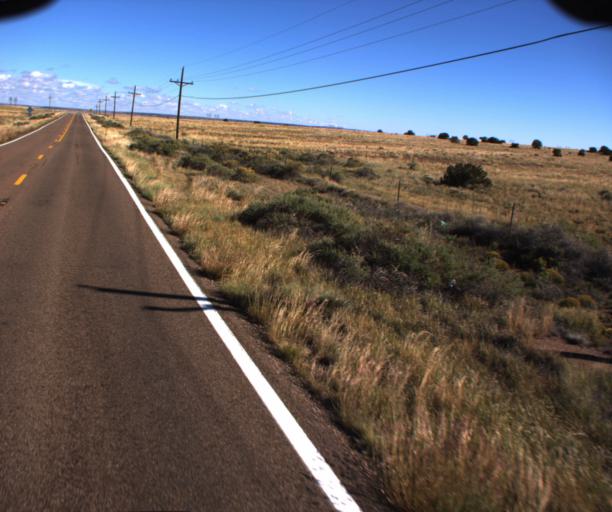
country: US
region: Arizona
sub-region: Apache County
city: Saint Johns
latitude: 34.5648
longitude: -109.3400
